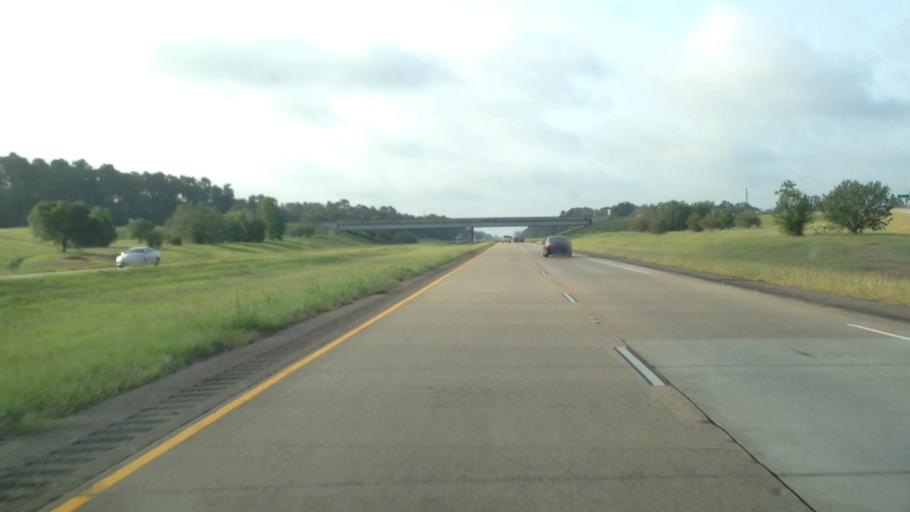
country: US
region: Louisiana
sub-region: Rapides Parish
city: Lecompte
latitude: 31.0743
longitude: -92.4352
